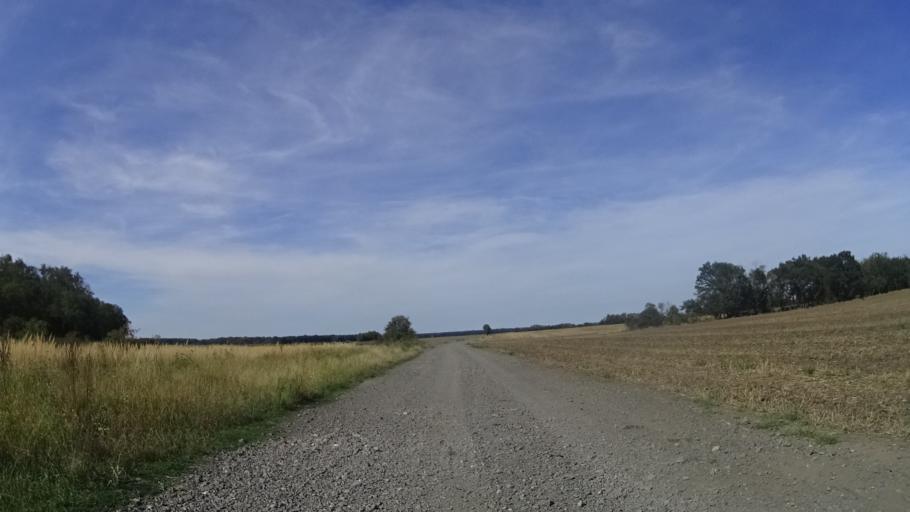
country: AT
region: Lower Austria
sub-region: Politischer Bezirk Ganserndorf
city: Durnkrut
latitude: 48.4316
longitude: 16.8690
